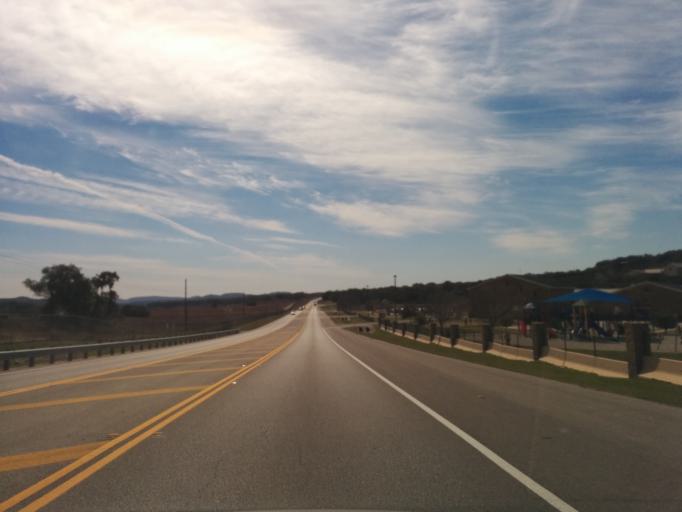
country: US
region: Texas
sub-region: Bexar County
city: Fair Oaks Ranch
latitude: 29.7300
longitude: -98.6235
